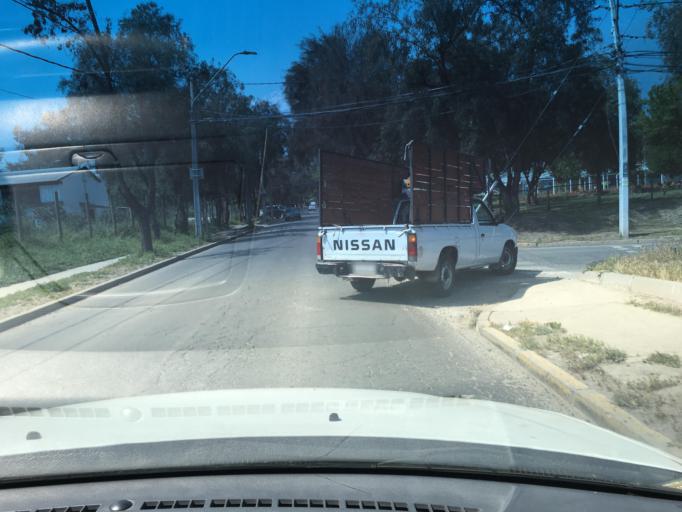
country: CL
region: Santiago Metropolitan
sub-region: Provincia de Santiago
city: Villa Presidente Frei, Nunoa, Santiago, Chile
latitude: -33.5146
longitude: -70.5489
